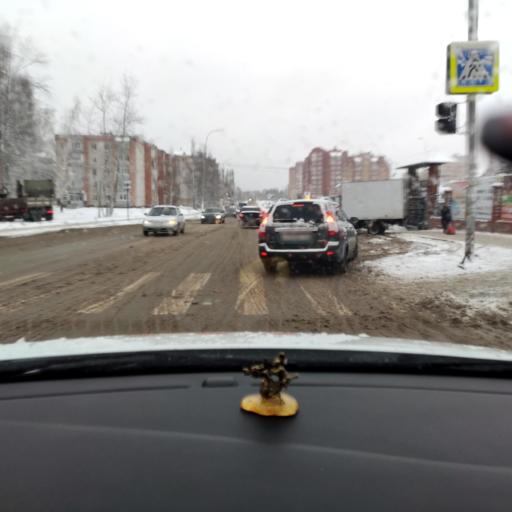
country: RU
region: Tatarstan
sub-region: Zelenodol'skiy Rayon
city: Zelenodolsk
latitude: 55.8565
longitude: 48.5602
